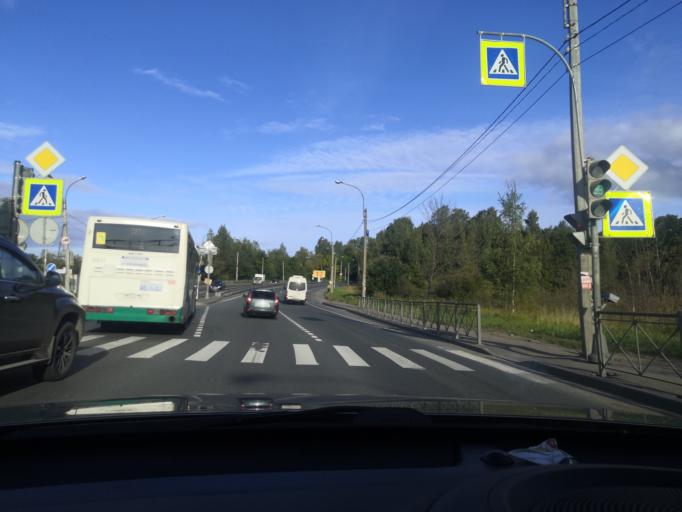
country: RU
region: St.-Petersburg
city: Pargolovo
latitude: 60.0788
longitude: 30.2673
